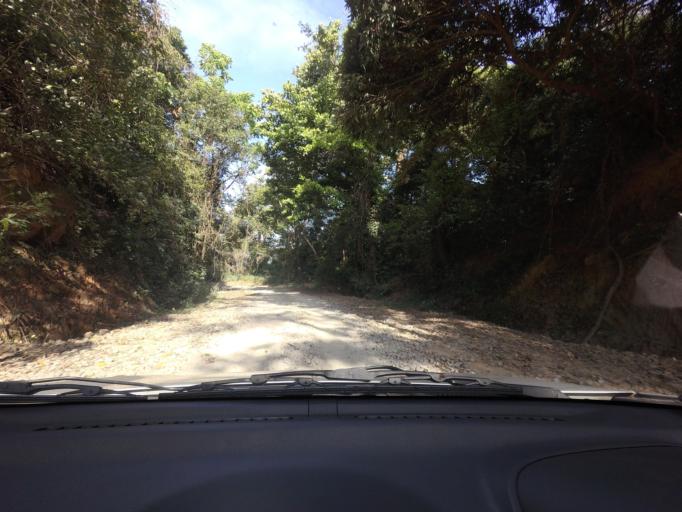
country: IN
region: Karnataka
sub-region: Kodagu
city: Somvarpet
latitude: 12.7117
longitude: 75.6694
